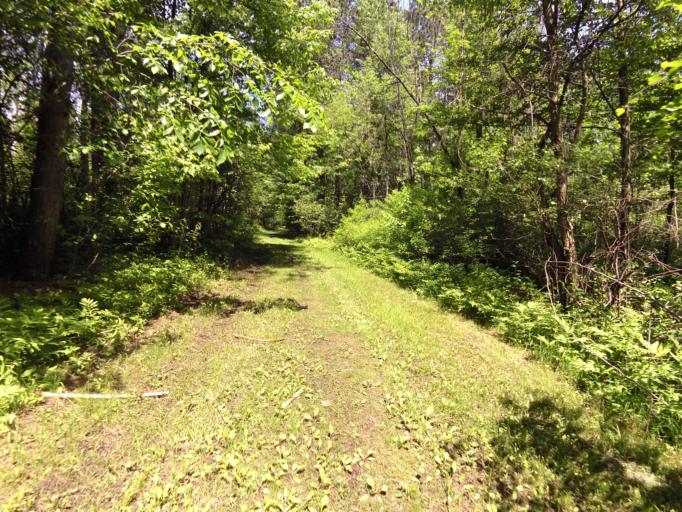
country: CA
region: Ontario
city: Ottawa
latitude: 45.3509
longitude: -75.6033
